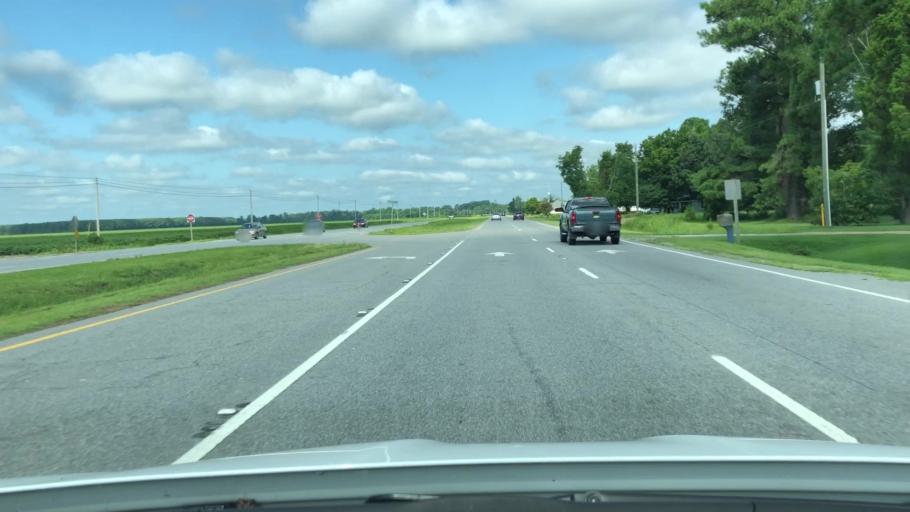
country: US
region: North Carolina
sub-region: Perquimans County
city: Hertford
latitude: 36.2080
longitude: -76.4075
